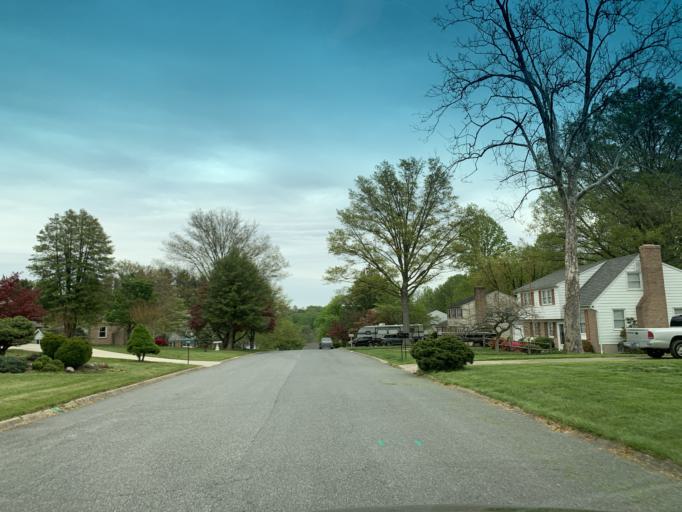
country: US
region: Maryland
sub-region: Harford County
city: South Bel Air
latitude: 39.5238
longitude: -76.3213
